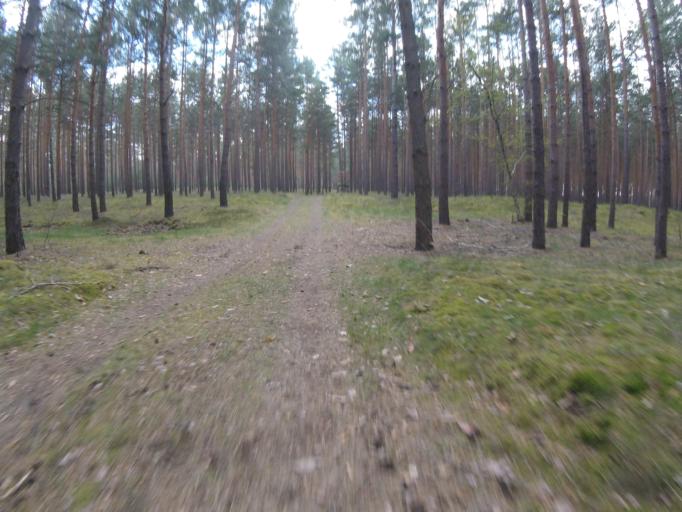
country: DE
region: Brandenburg
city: Gross Koris
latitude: 52.1848
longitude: 13.6843
